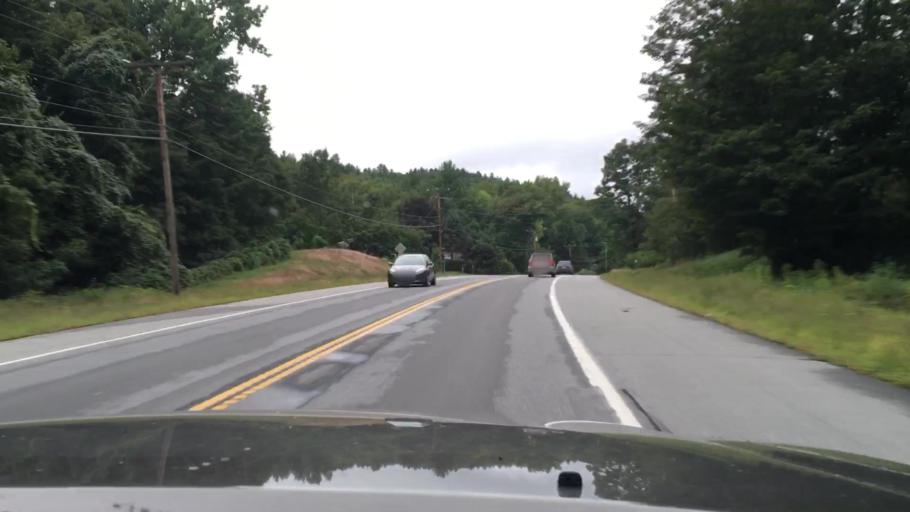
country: US
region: Vermont
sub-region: Windham County
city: Brattleboro
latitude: 42.8896
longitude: -72.5292
